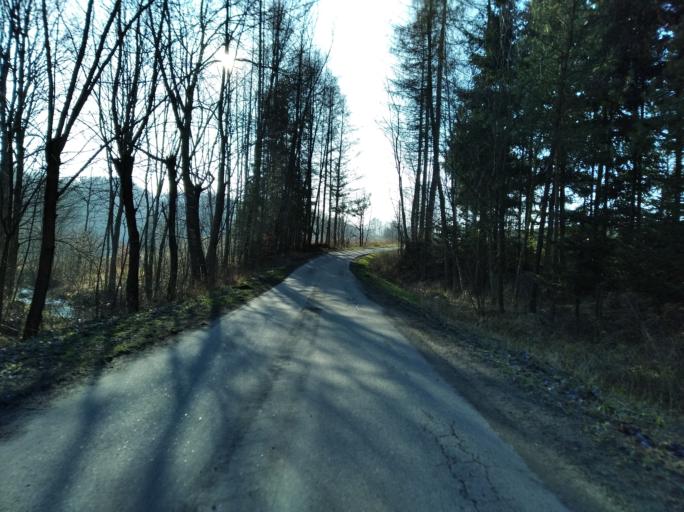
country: PL
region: Subcarpathian Voivodeship
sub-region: Powiat strzyzowski
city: Konieczkowa
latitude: 49.8547
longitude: 21.9281
